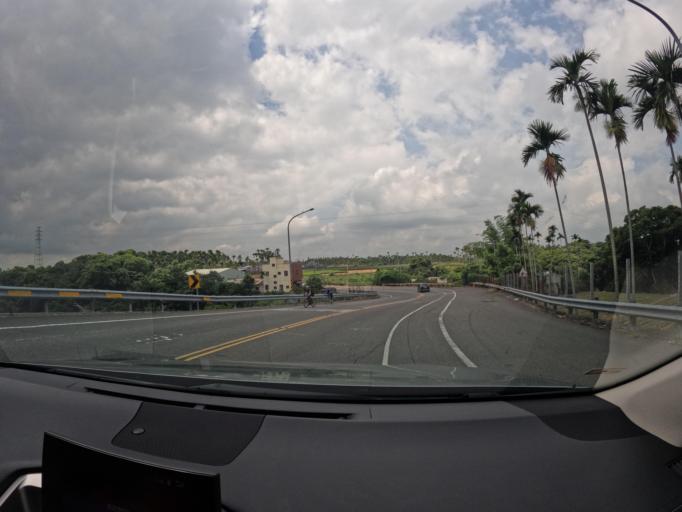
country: TW
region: Taiwan
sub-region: Nantou
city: Nantou
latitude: 23.9230
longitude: 120.6379
